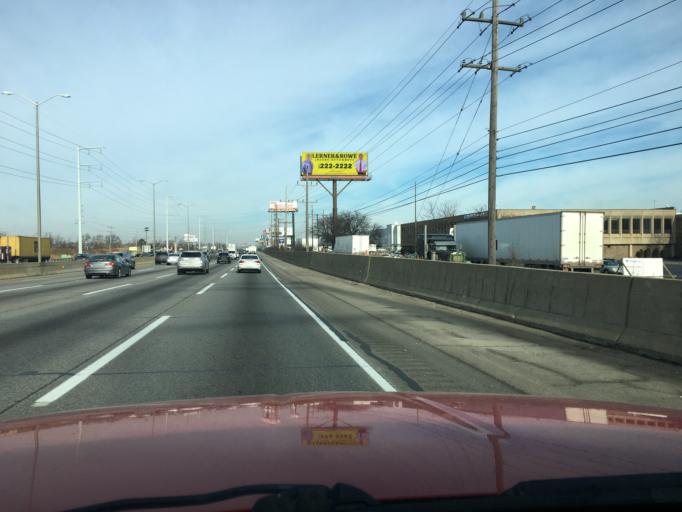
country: US
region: Illinois
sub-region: DuPage County
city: Elmhurst
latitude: 41.9121
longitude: -87.9196
